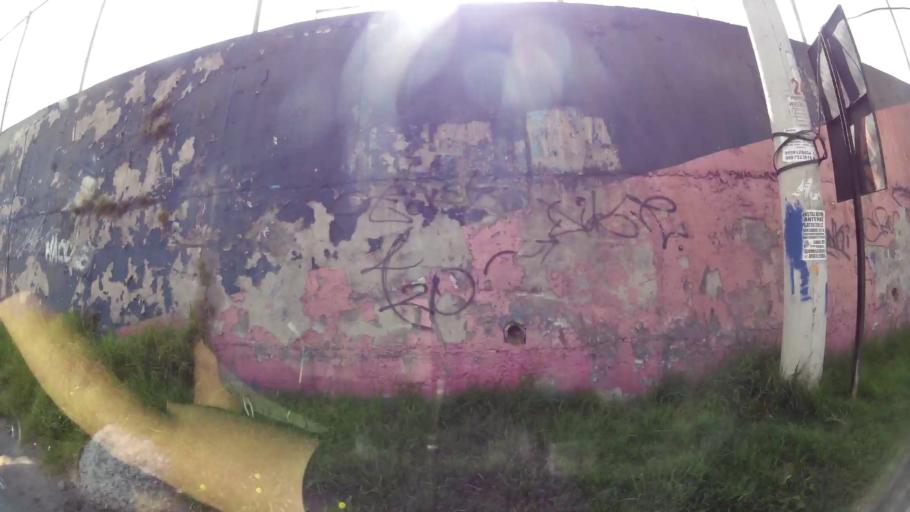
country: EC
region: Pichincha
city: Quito
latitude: -0.1089
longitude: -78.4745
